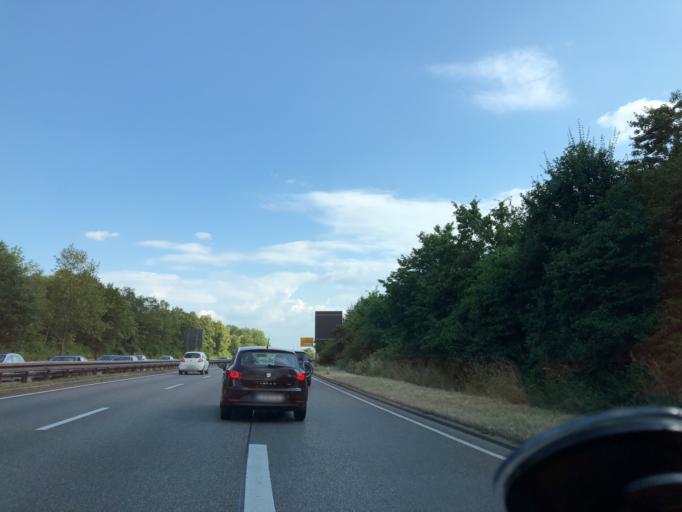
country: DE
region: Baden-Wuerttemberg
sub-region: Regierungsbezirk Stuttgart
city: Stuttgart
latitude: 48.7420
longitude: 9.1613
